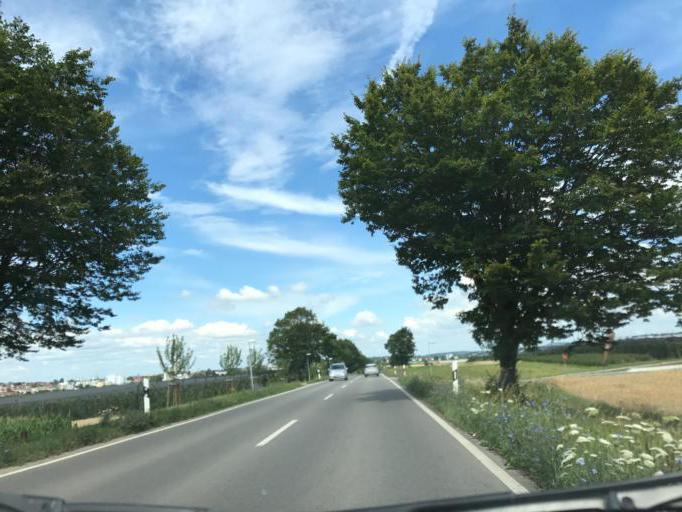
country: DE
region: Baden-Wuerttemberg
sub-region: Regierungsbezirk Stuttgart
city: Weinstadt-Endersbach
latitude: 48.7977
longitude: 9.3376
